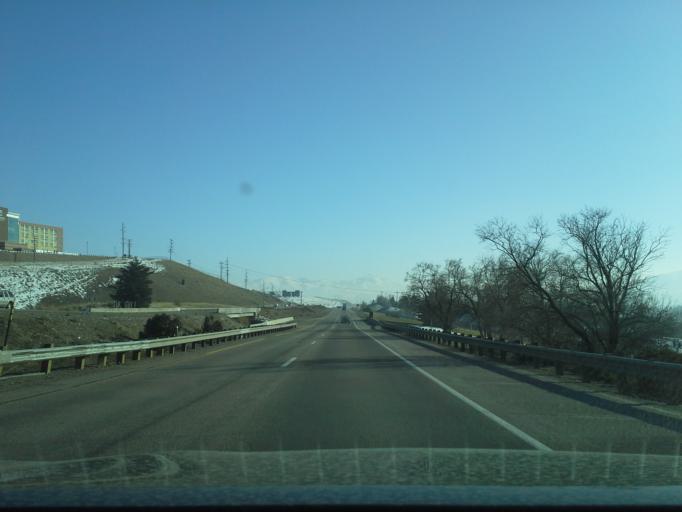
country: US
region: Idaho
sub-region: Bannock County
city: Pocatello
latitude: 42.8767
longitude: -112.4259
